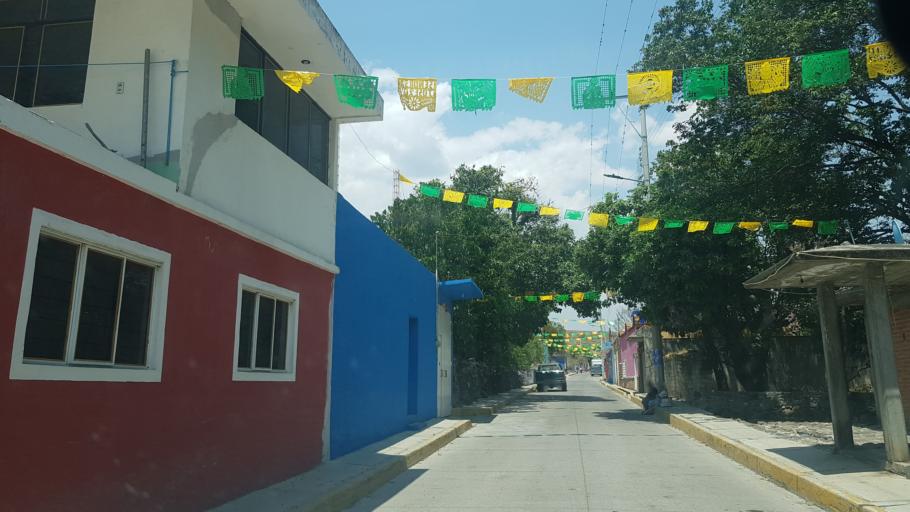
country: MX
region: Puebla
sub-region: Atzitzihuacan
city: Santiago Atzitzihuacan
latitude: 18.8240
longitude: -98.5819
